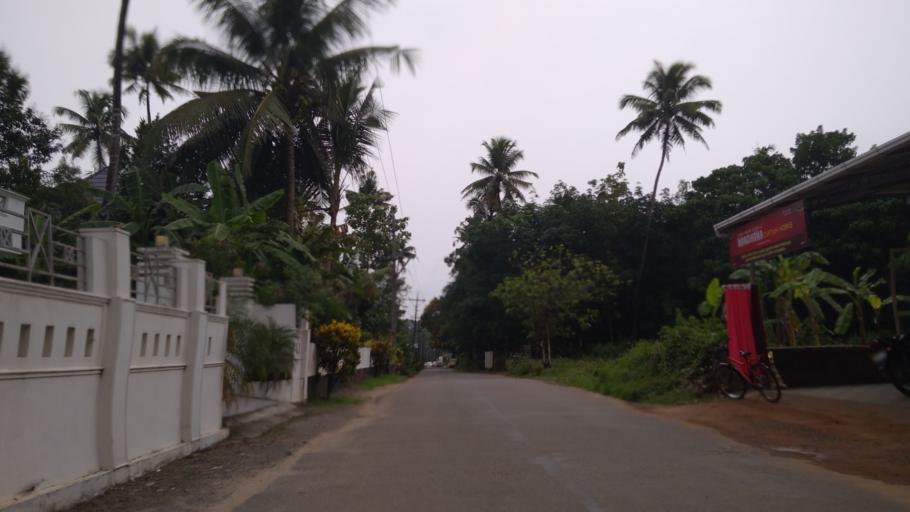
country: IN
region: Kerala
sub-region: Ernakulam
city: Kotamangalam
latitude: 10.1212
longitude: 76.5663
